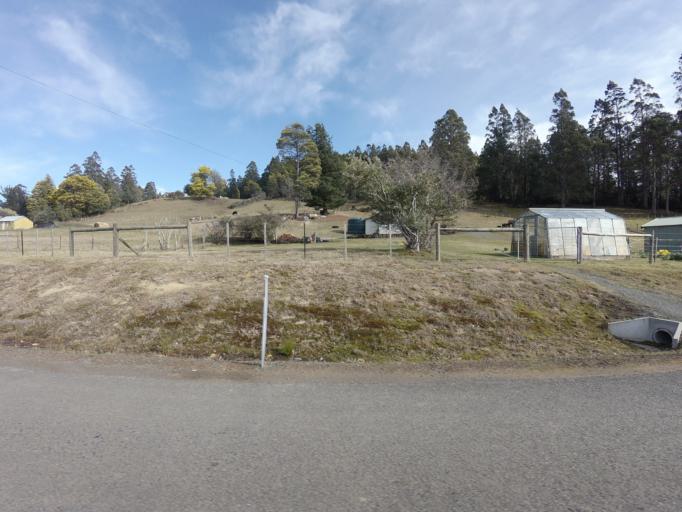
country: AU
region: Tasmania
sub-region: Kingborough
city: Margate
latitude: -43.0194
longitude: 147.1647
